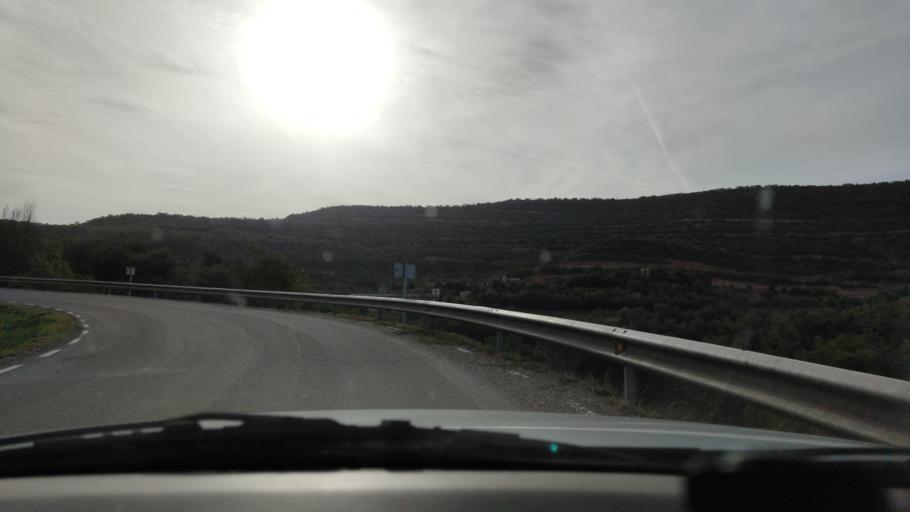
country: ES
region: Catalonia
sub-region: Provincia de Lleida
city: Artesa de Segre
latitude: 41.9146
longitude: 1.1134
